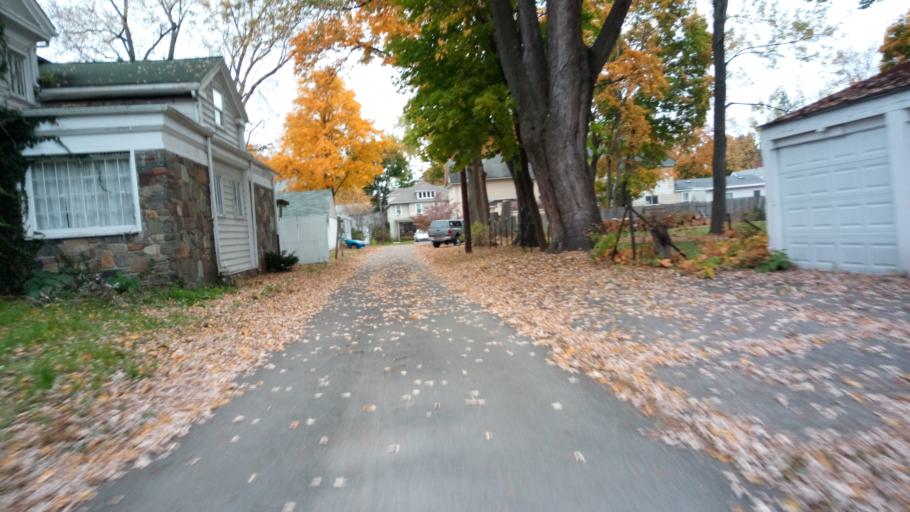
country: US
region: New York
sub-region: Chemung County
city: Elmira
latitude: 42.0806
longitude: -76.7939
